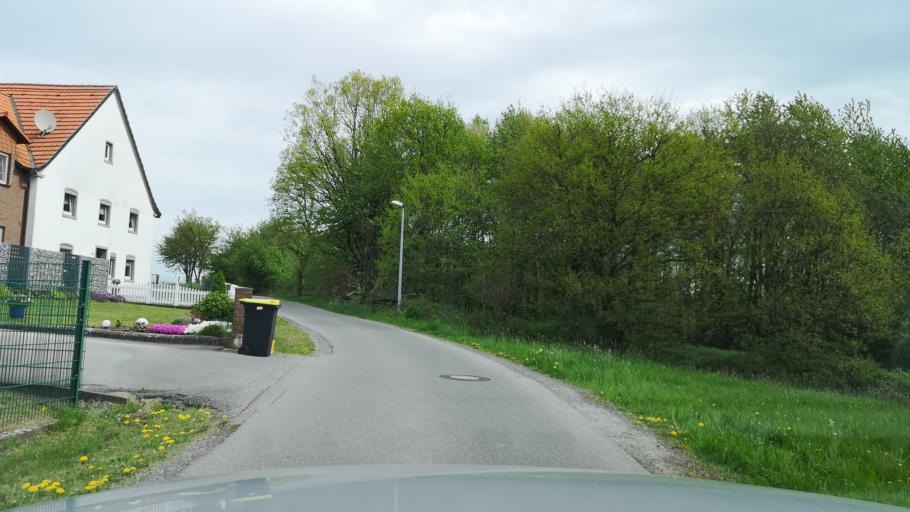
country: DE
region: North Rhine-Westphalia
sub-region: Regierungsbezirk Arnsberg
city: Frondenberg
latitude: 51.4859
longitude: 7.7876
